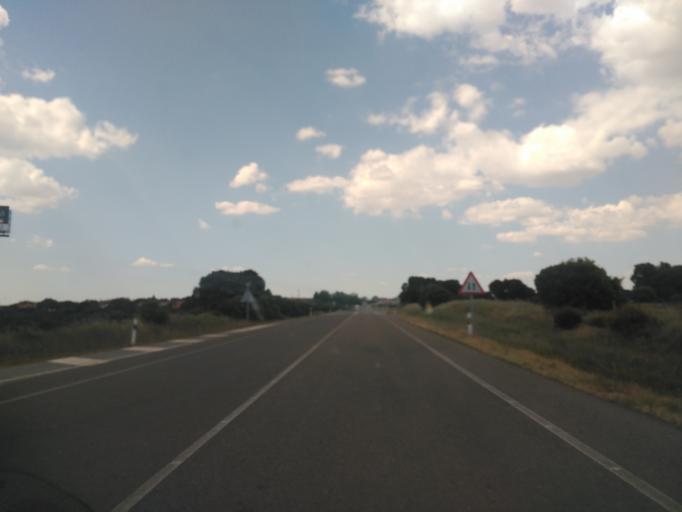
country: ES
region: Castille and Leon
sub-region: Provincia de Salamanca
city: Martinamor
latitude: 40.8013
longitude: -5.6330
